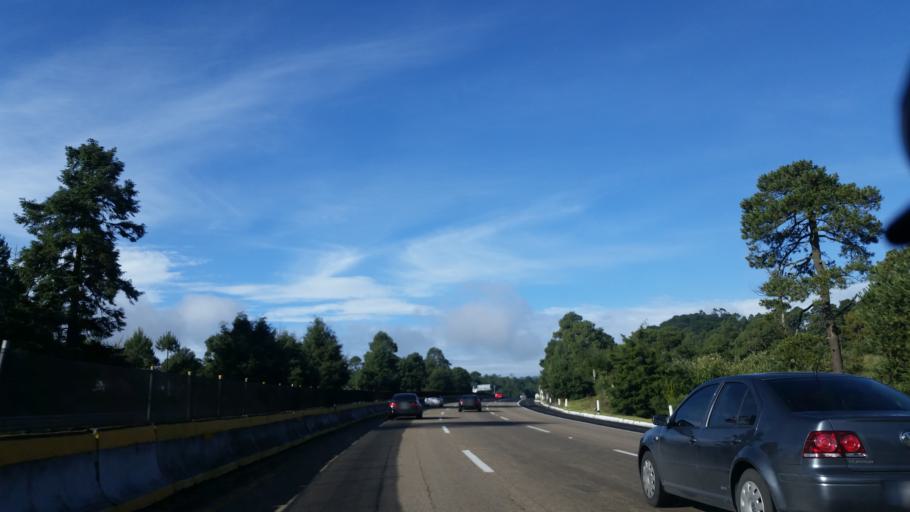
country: MX
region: Morelos
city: Tres Marias
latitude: 19.1144
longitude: -99.1829
